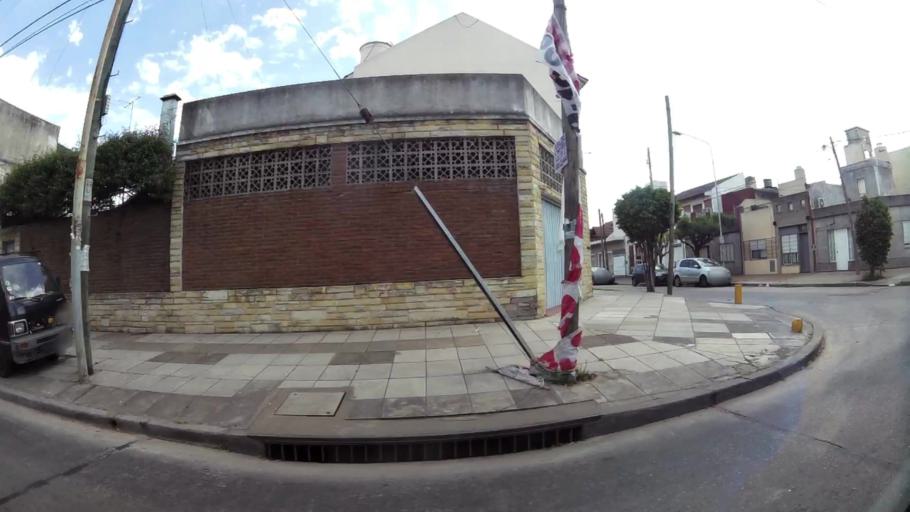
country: AR
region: Buenos Aires
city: San Justo
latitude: -34.6557
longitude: -58.5694
